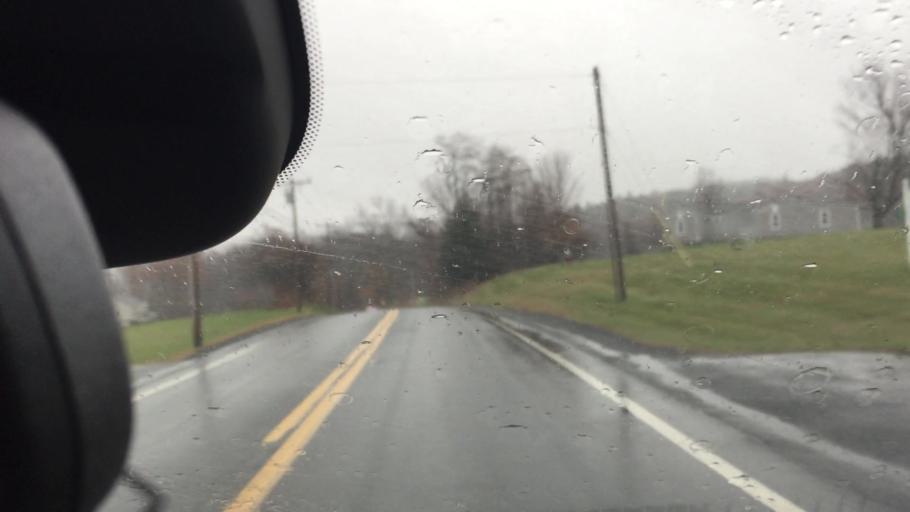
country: US
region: Massachusetts
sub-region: Hampden County
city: Granville
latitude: 42.1740
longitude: -72.9145
